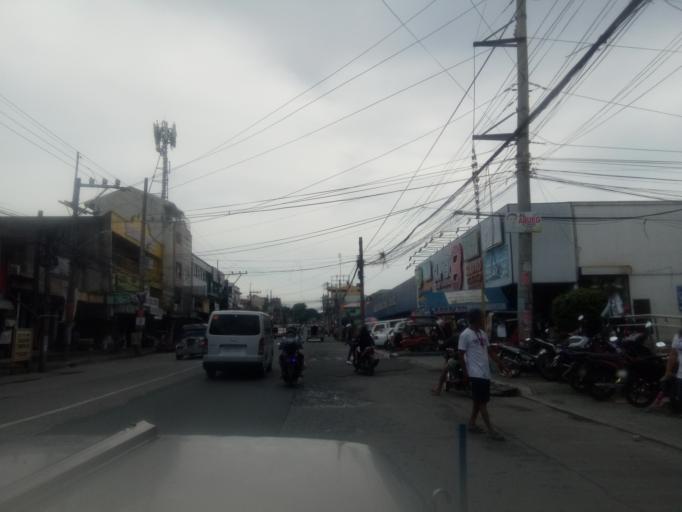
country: PH
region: Calabarzon
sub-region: Province of Cavite
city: Bulihan
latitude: 14.2942
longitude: 121.0065
